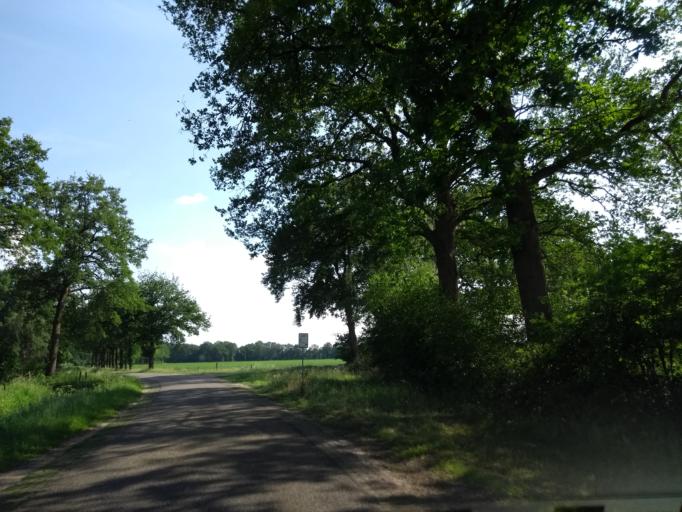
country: DE
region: Lower Saxony
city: Nordhorn
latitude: 52.3739
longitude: 7.0324
